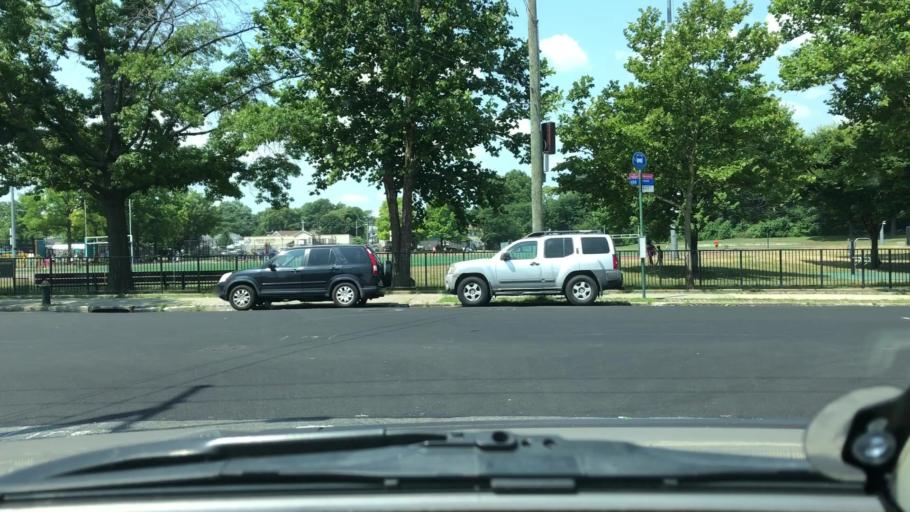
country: US
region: New Jersey
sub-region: Hudson County
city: Bayonne
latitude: 40.6381
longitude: -74.1175
